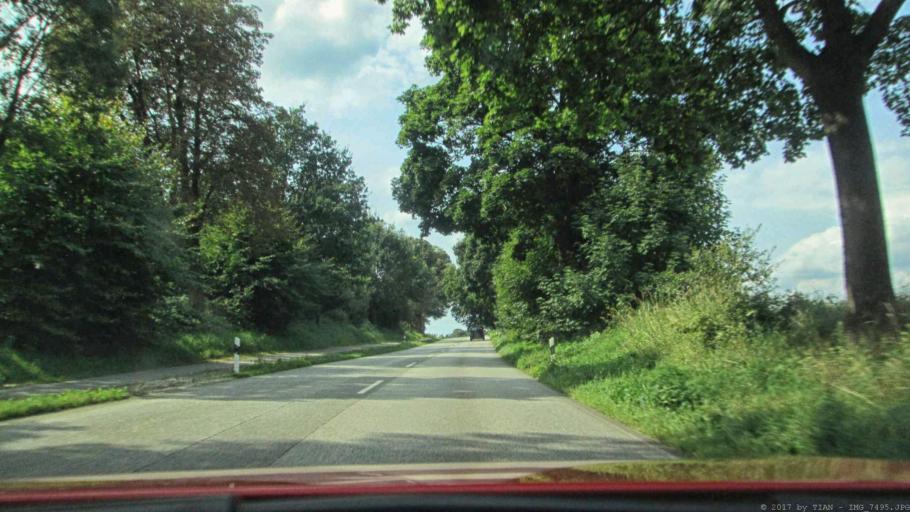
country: DE
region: Schleswig-Holstein
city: Kruzen
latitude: 53.3739
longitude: 10.5277
